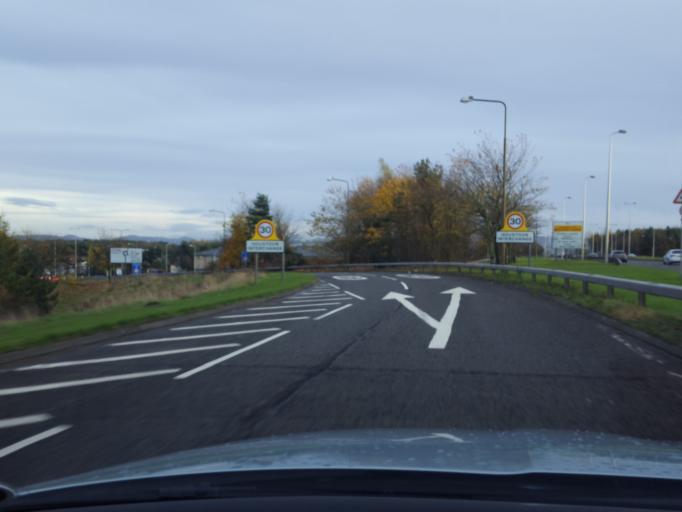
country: GB
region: Scotland
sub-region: West Lothian
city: Livingston
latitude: 55.9071
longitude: -3.5166
